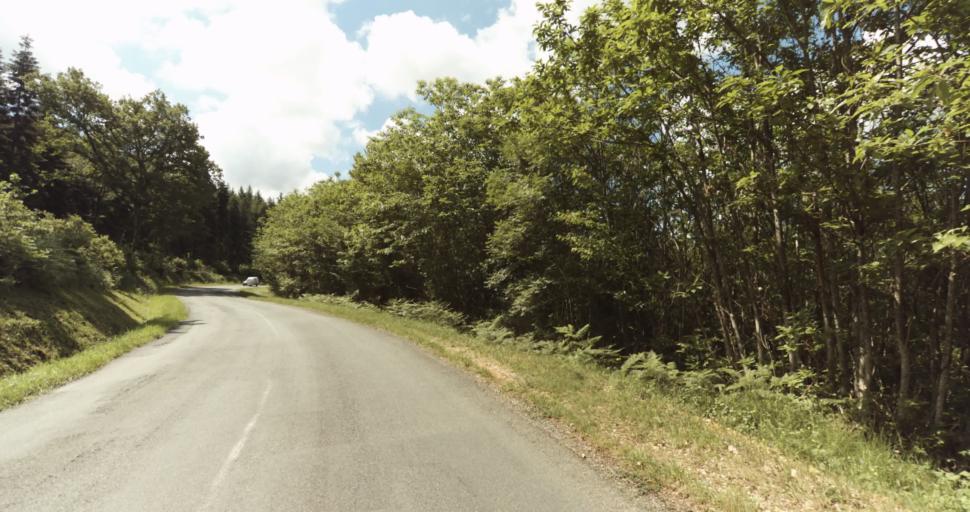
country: FR
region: Aquitaine
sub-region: Departement de la Dordogne
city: Beaumont-du-Perigord
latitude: 44.8119
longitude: 0.8571
